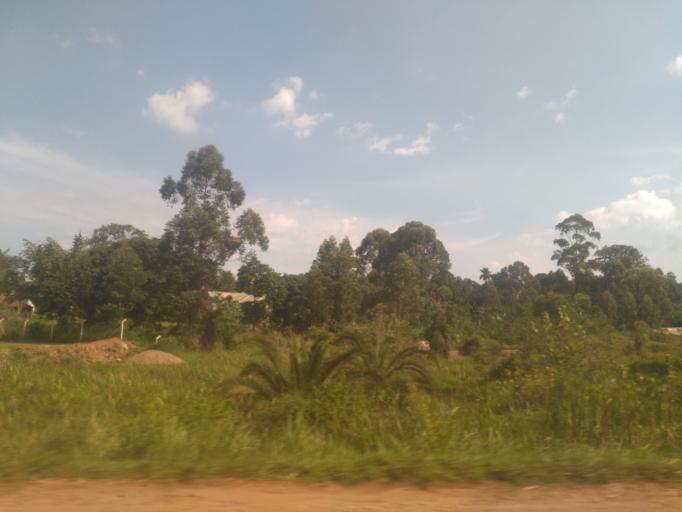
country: UG
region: Central Region
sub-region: Wakiso District
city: Kajansi
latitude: 0.2815
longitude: 32.4839
